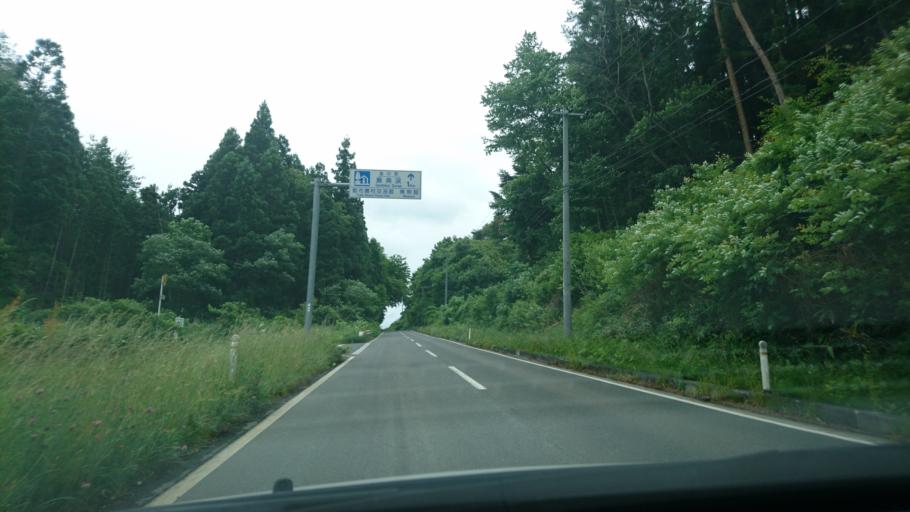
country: JP
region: Iwate
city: Ichinoseki
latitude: 38.9564
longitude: 141.0540
